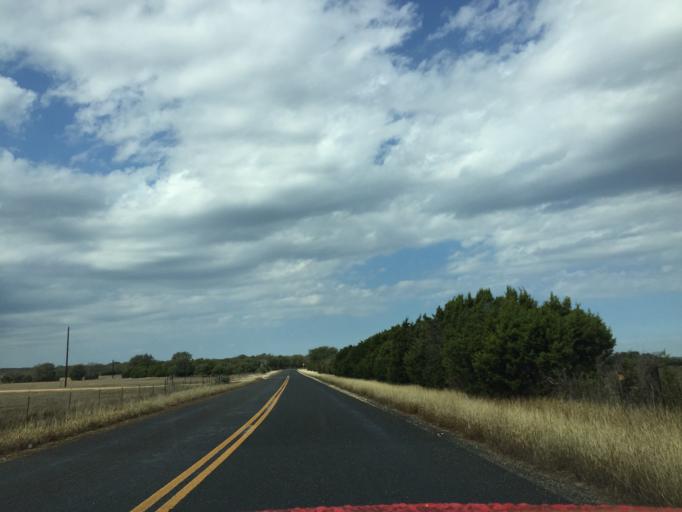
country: US
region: Texas
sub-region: Burnet County
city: Bertram
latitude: 30.6281
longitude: -97.9925
